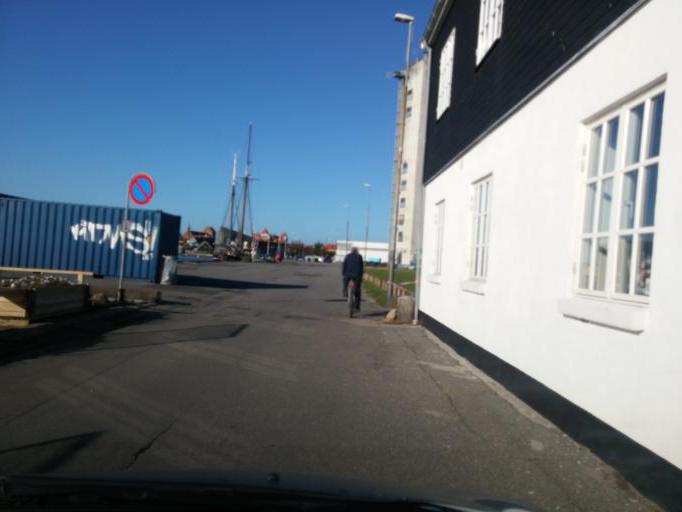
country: DK
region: South Denmark
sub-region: Kerteminde Kommune
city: Kerteminde
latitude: 55.4509
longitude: 10.6653
